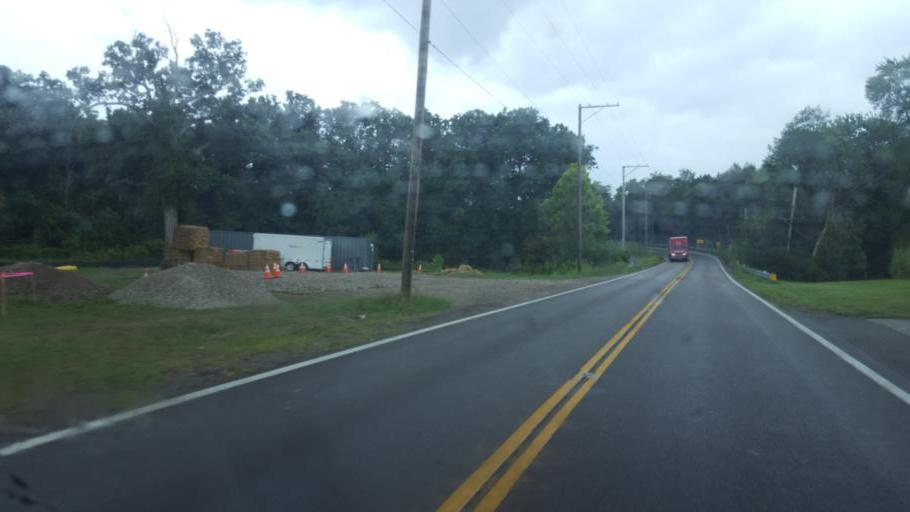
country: US
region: Ohio
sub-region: Delaware County
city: Delaware
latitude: 40.3105
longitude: -83.0543
